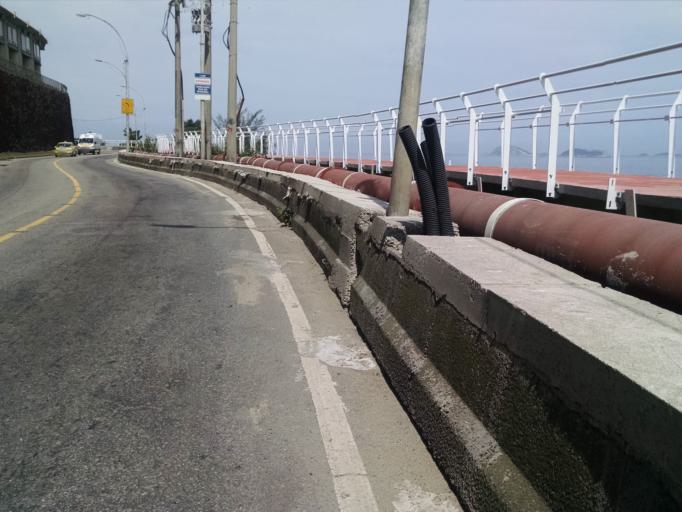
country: BR
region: Rio de Janeiro
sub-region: Rio De Janeiro
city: Rio de Janeiro
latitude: -23.0006
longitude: -43.2451
